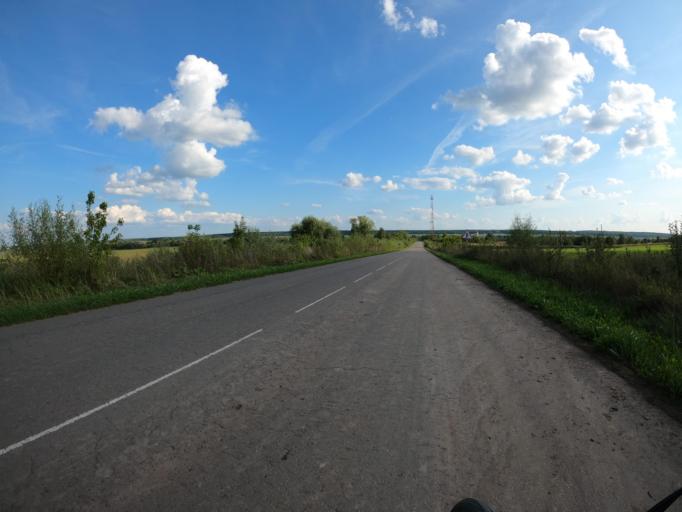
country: RU
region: Moskovskaya
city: Troitskoye
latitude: 55.2010
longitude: 38.4887
